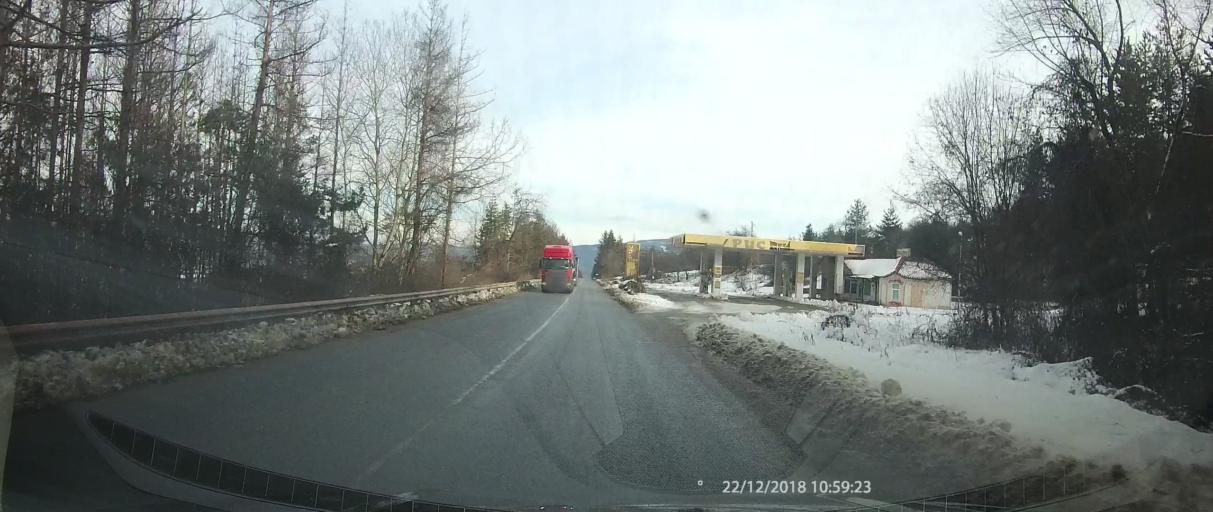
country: MK
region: Kriva Palanka
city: Kriva Palanka
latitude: 42.2242
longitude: 22.4799
